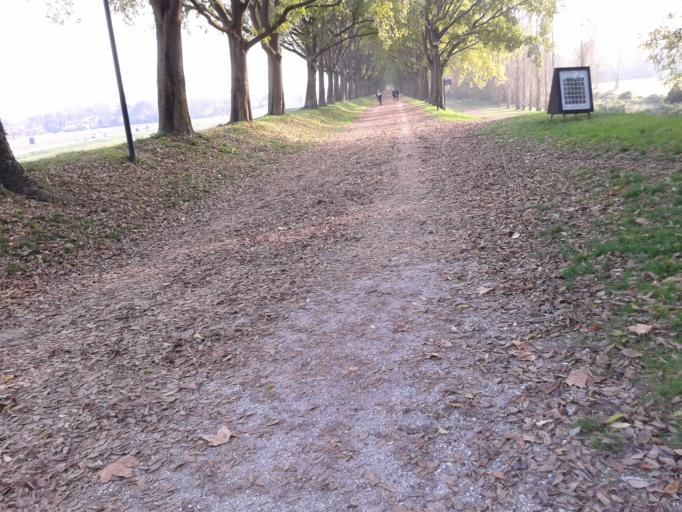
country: IT
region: Emilia-Romagna
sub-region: Provincia di Ferrara
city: Ferrara
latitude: 44.8482
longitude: 11.6322
